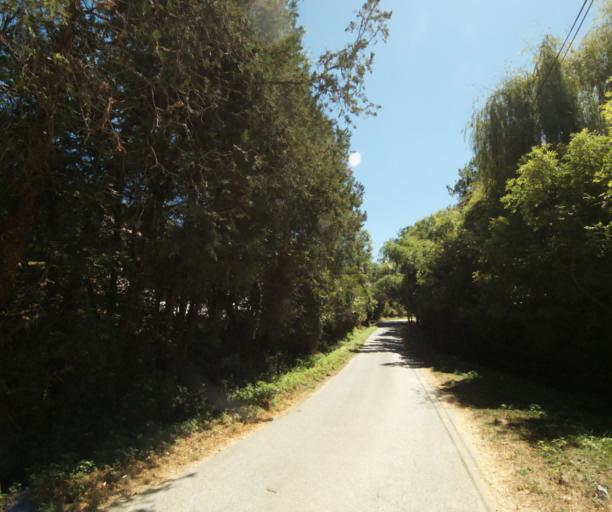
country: FR
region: Midi-Pyrenees
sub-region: Departement de la Haute-Garonne
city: Castanet-Tolosan
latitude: 43.5081
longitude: 1.4945
